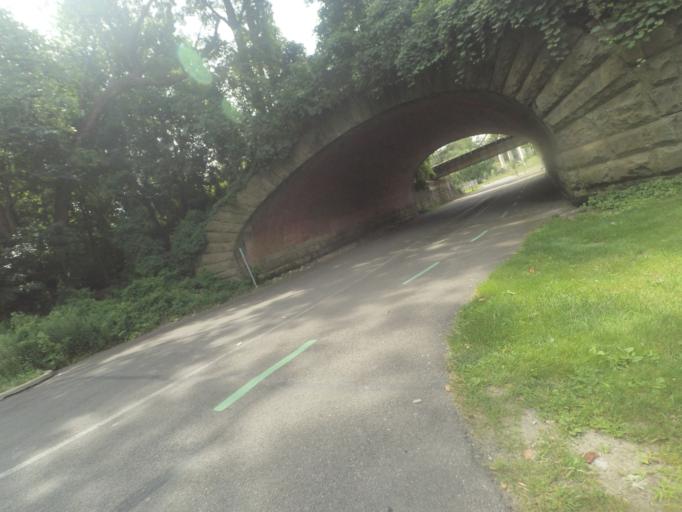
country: US
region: Ohio
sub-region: Cuyahoga County
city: Brooklyn
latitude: 41.4507
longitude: -81.7162
